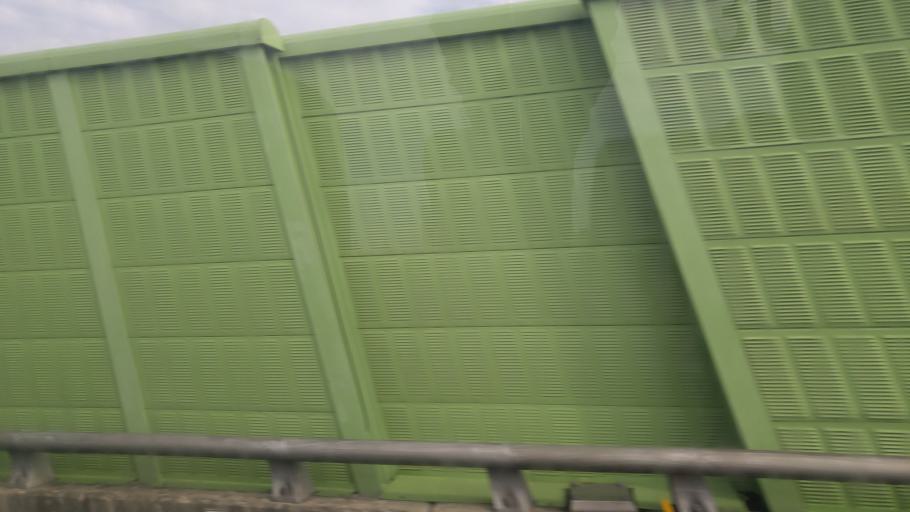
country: TW
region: Taiwan
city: Daxi
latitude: 24.9219
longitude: 121.1695
